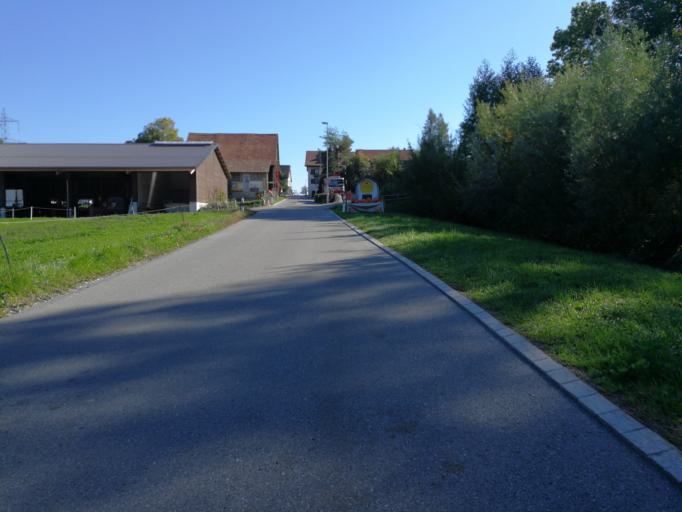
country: CH
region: Zurich
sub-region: Bezirk Uster
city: Aesch
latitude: 47.3231
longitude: 8.6679
